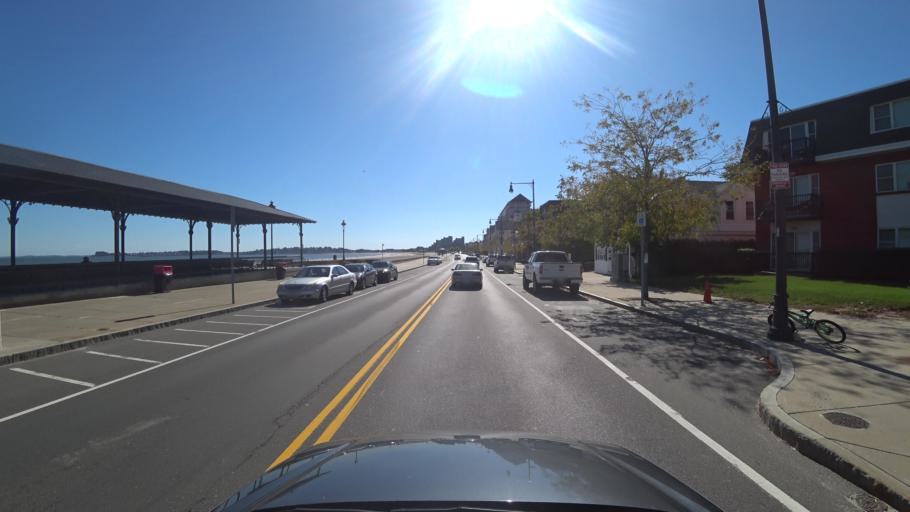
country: US
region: Massachusetts
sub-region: Suffolk County
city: Revere
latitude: 42.4231
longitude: -70.9841
